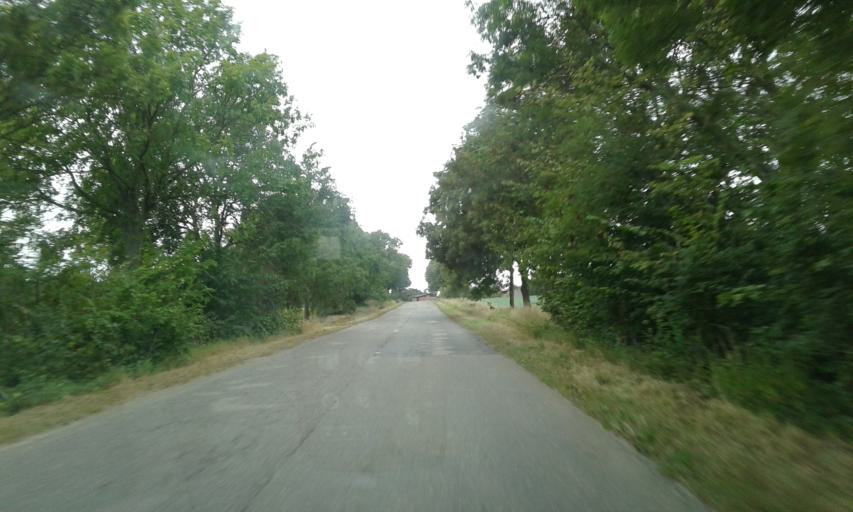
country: PL
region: West Pomeranian Voivodeship
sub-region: Powiat pyrzycki
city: Warnice
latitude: 53.1841
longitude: 15.0218
